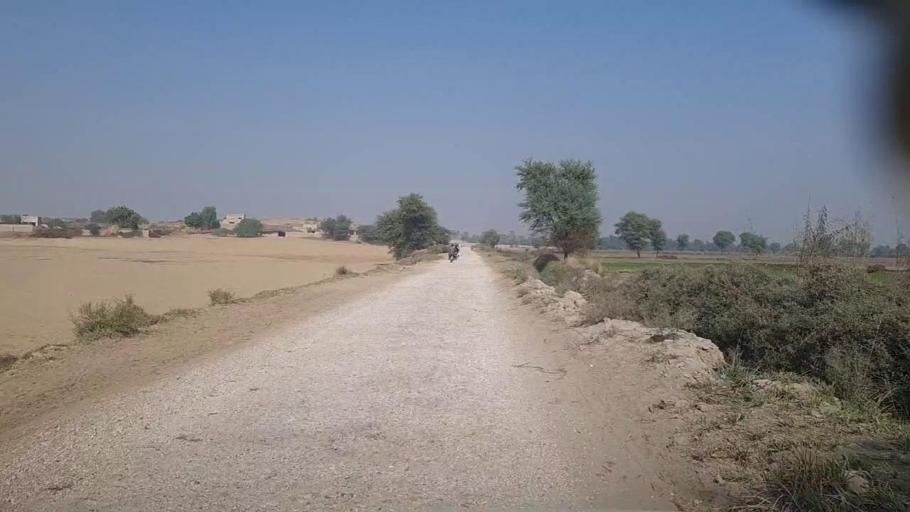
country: PK
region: Sindh
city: Kandiari
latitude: 26.9234
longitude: 68.5181
